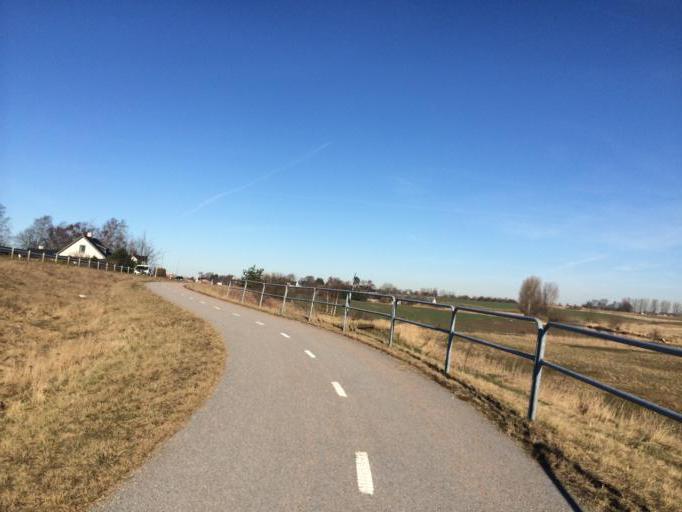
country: SE
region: Skane
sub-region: Kavlinge Kommun
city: Loddekopinge
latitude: 55.7514
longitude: 13.0273
